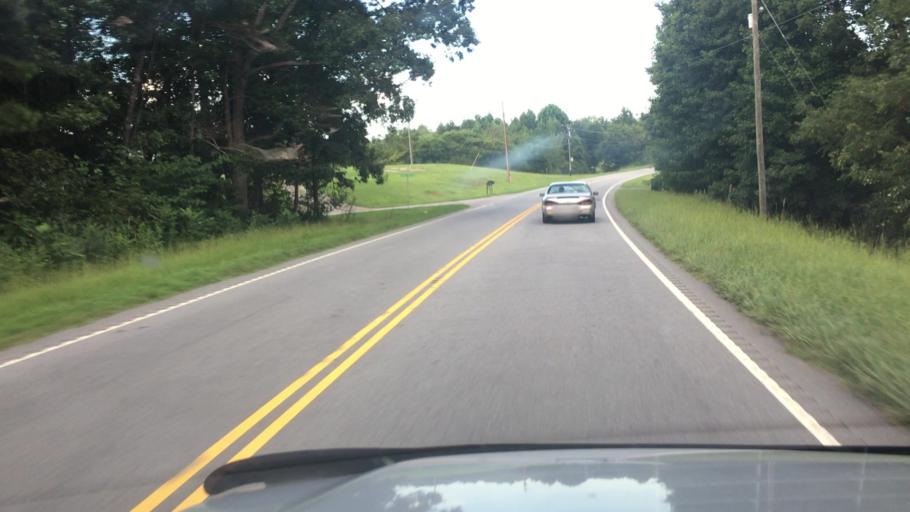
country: US
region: South Carolina
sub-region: Cherokee County
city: Gaffney
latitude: 35.1295
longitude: -81.7491
